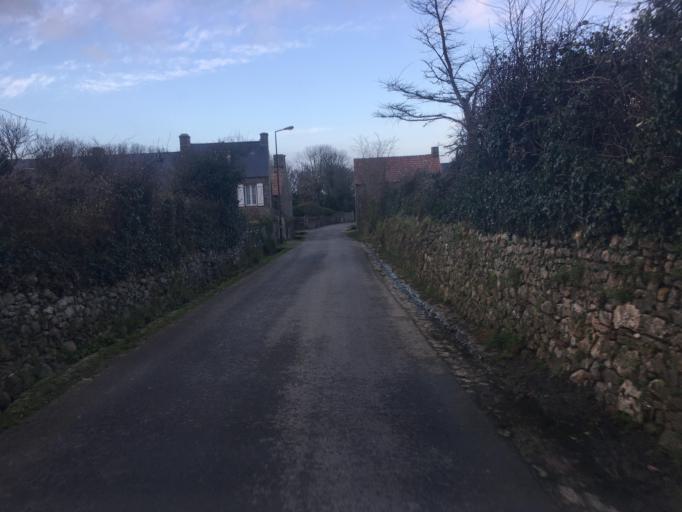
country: FR
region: Lower Normandy
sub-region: Departement de la Manche
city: Beaumont-Hague
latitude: 49.7135
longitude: -1.9220
